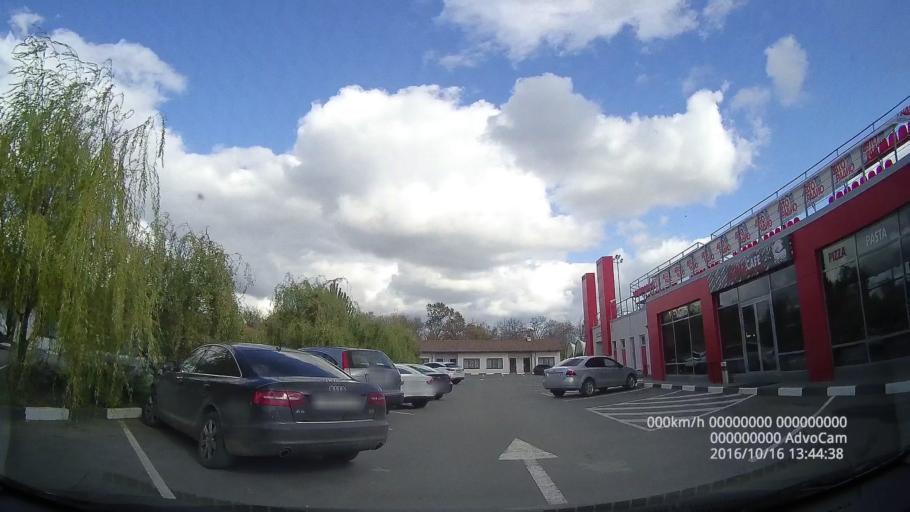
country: RU
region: Rostov
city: Bataysk
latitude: 47.1148
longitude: 39.6613
